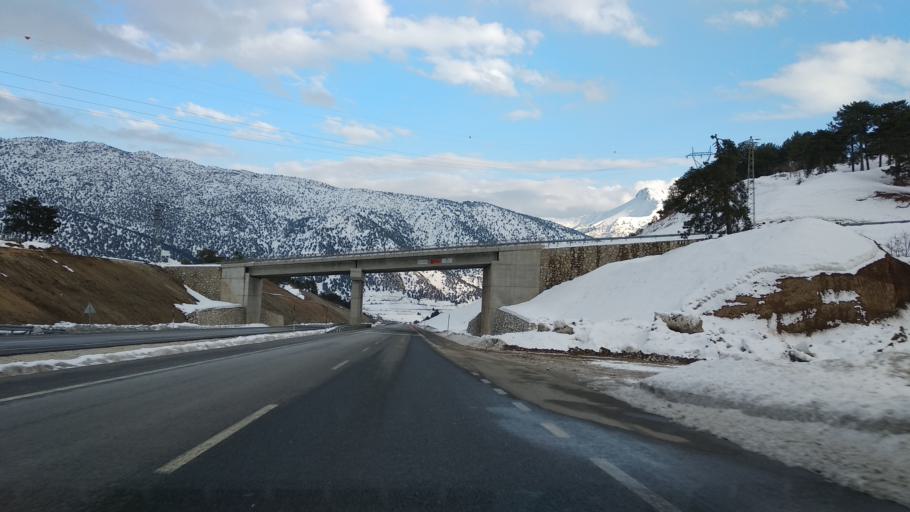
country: TR
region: Kahramanmaras
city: Goksun
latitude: 37.9054
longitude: 36.5965
